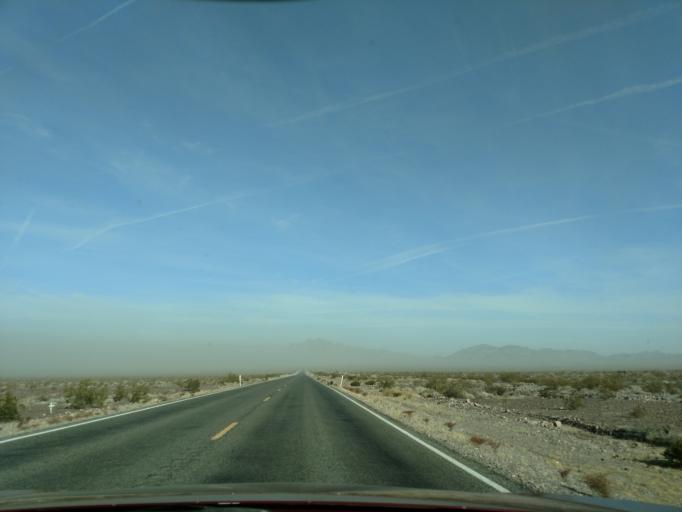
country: US
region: Nevada
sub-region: Nye County
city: Pahrump
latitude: 36.5138
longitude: -116.1193
